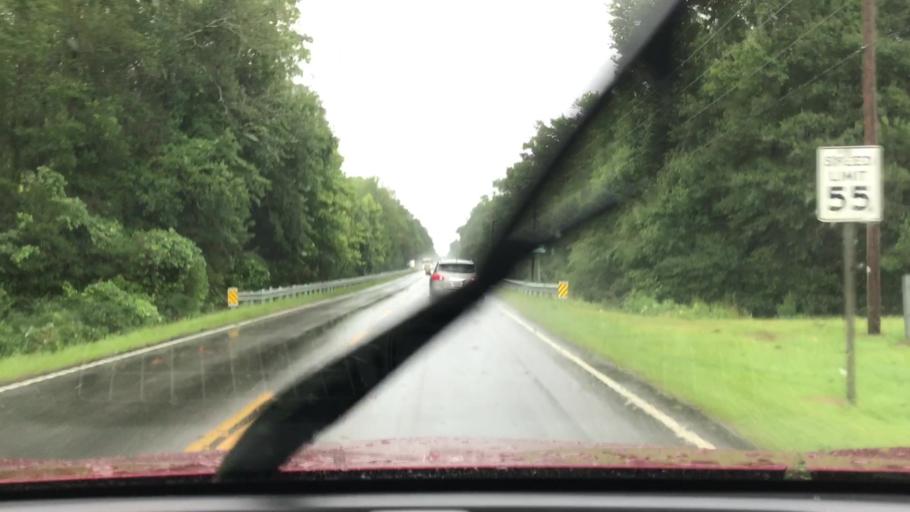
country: US
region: South Carolina
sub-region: Horry County
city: Conway
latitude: 33.7492
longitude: -79.0781
